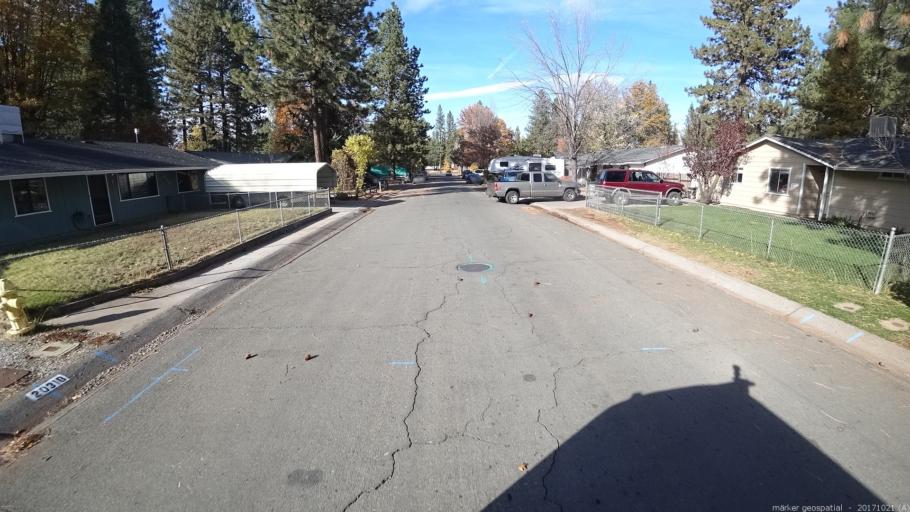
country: US
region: California
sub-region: Shasta County
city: Burney
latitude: 40.8797
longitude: -121.6549
